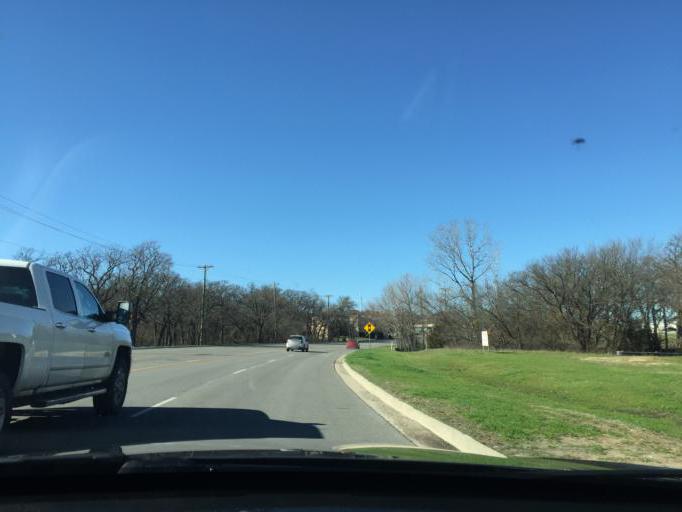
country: US
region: Texas
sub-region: Parker County
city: Weatherford
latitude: 32.7403
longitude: -97.7803
